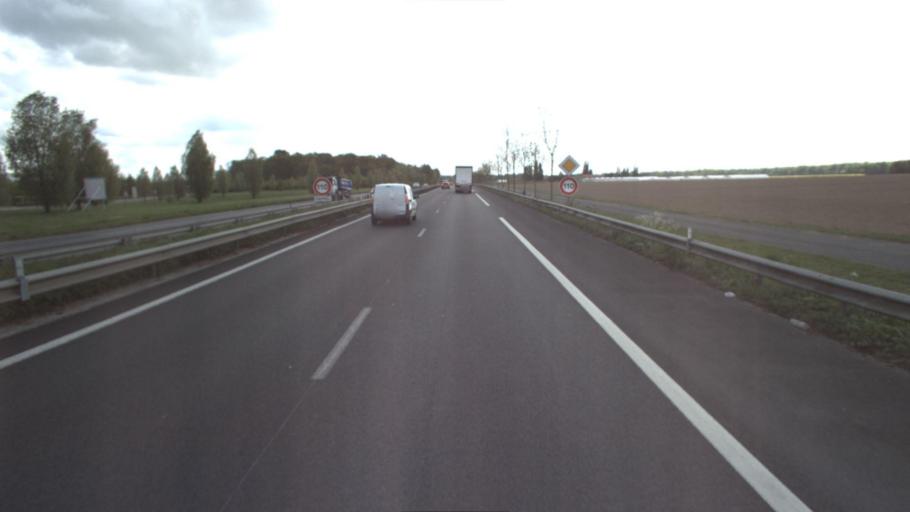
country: FR
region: Ile-de-France
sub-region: Departement de Seine-et-Marne
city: Neufmoutiers-en-Brie
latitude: 48.7260
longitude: 2.8206
